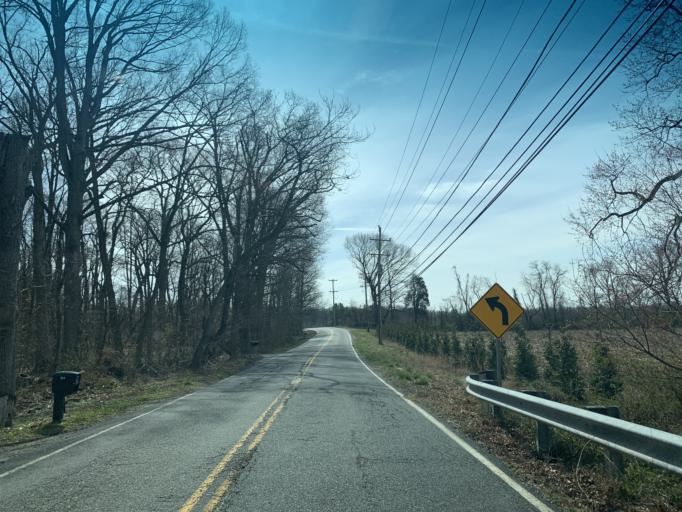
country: US
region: Maryland
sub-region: Cecil County
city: Charlestown
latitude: 39.5619
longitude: -76.0200
